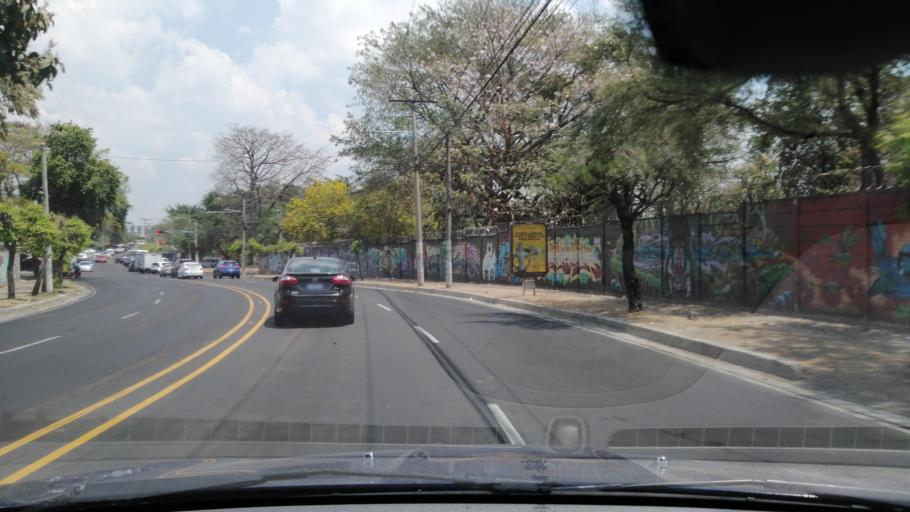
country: SV
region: San Salvador
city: San Salvador
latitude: 13.7046
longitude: -89.2033
